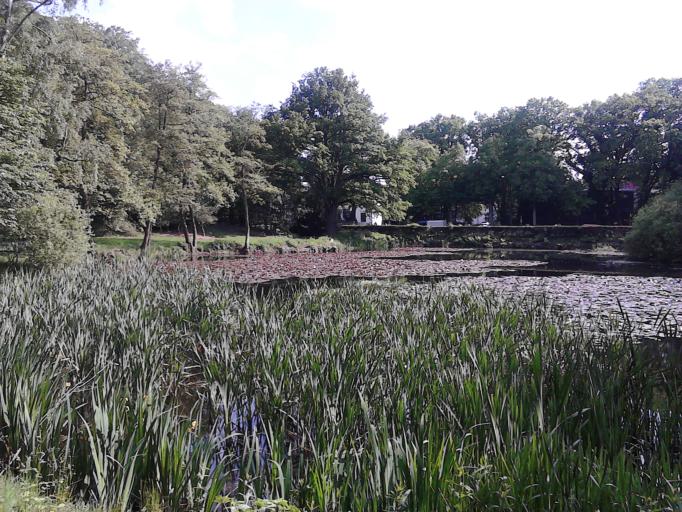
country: DE
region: Lower Saxony
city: Lilienthal
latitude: 53.0915
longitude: 8.8808
